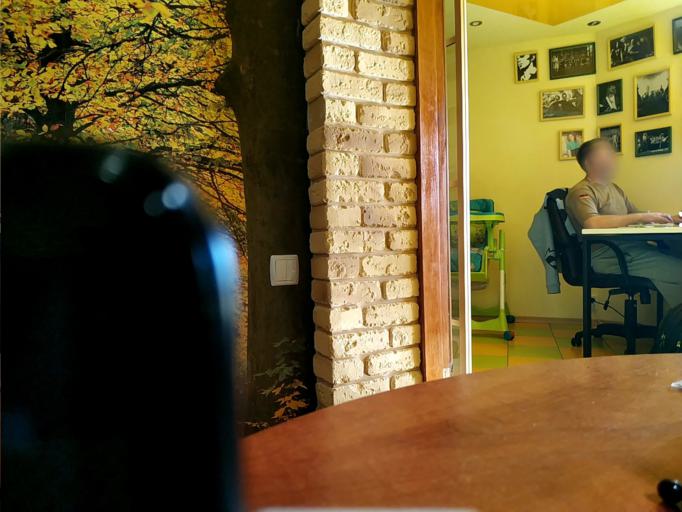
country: RU
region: Tverskaya
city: Vasil'yevskiy Mokh
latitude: 57.1575
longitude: 35.8166
